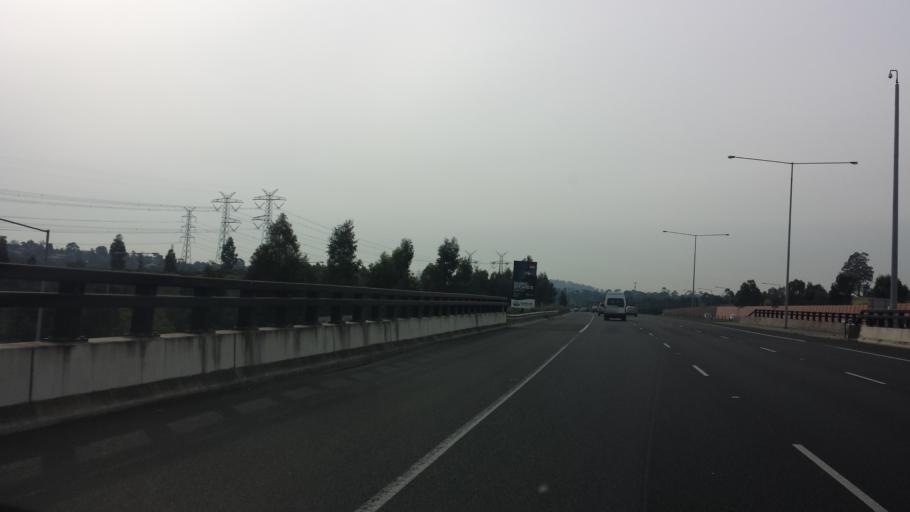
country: AU
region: Victoria
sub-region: Knox
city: Wantirna
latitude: -37.8465
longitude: 145.2169
